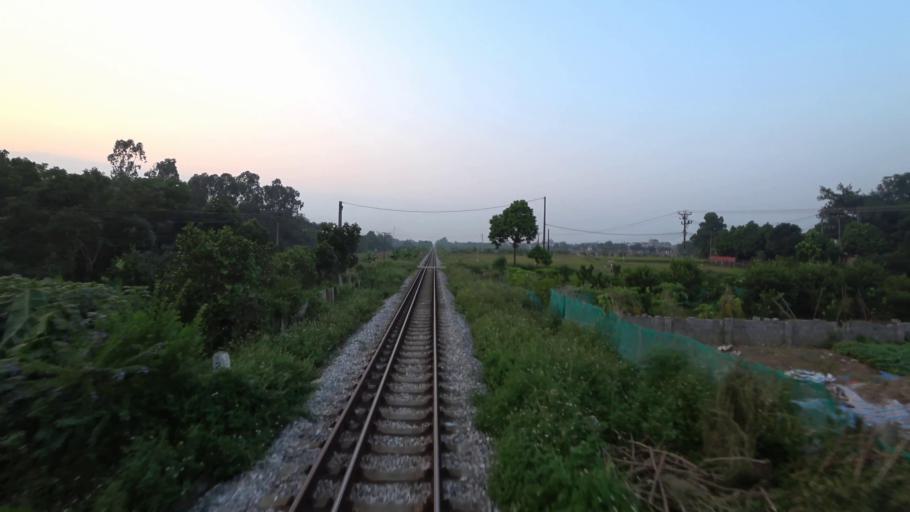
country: VN
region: Ha Noi
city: Dong Anh
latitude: 21.1324
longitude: 105.8740
